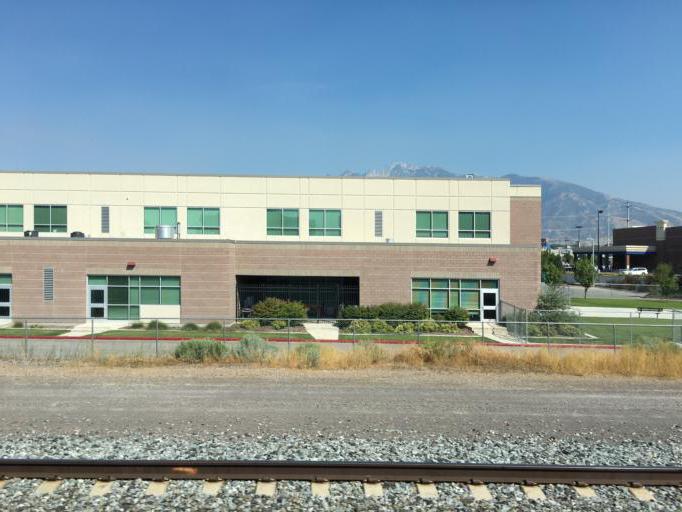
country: US
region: Utah
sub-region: Salt Lake County
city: South Jordan
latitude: 40.5487
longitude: -111.9024
